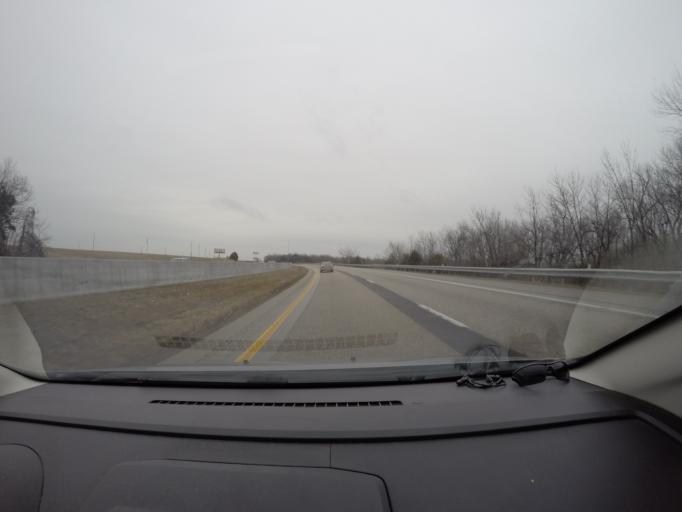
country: US
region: Missouri
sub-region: Gasconade County
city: Hermann
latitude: 38.8669
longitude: -91.3543
